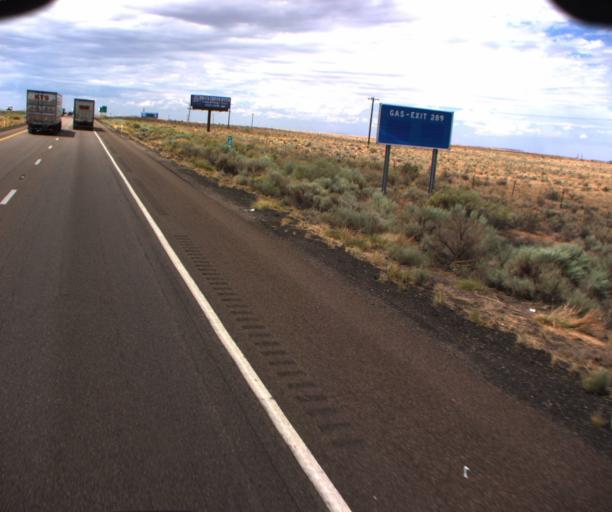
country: US
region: Arizona
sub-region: Navajo County
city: Holbrook
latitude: 34.9460
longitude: -110.1230
